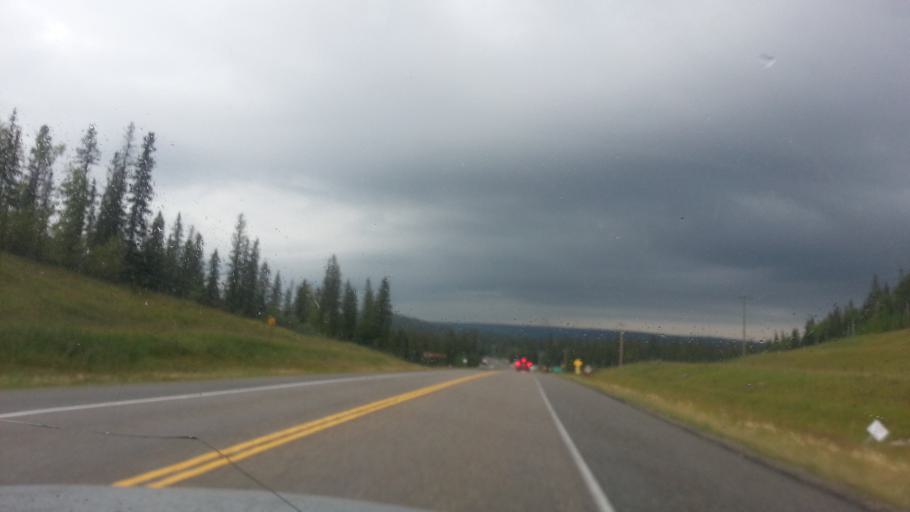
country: CA
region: Alberta
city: Cochrane
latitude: 50.9474
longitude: -114.5605
